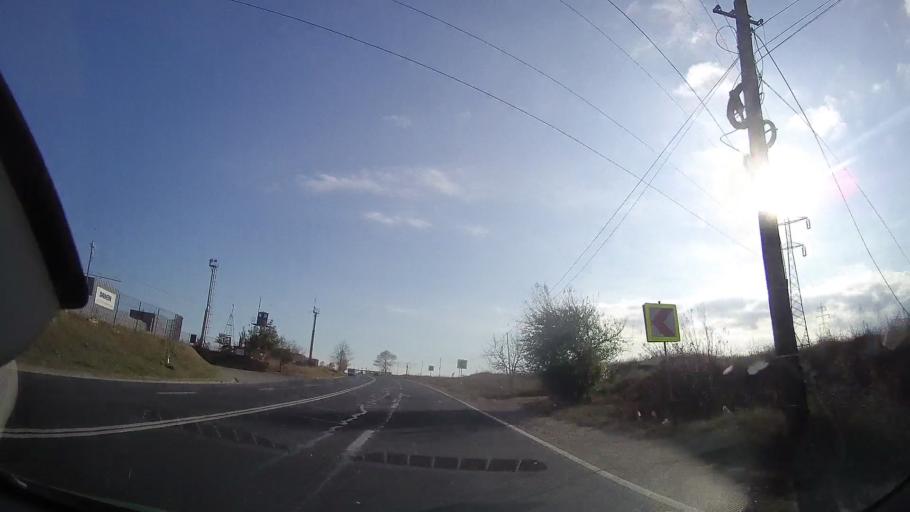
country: RO
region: Constanta
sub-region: Municipiul Mangalia
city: Mangalia
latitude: 43.7987
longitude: 28.5592
